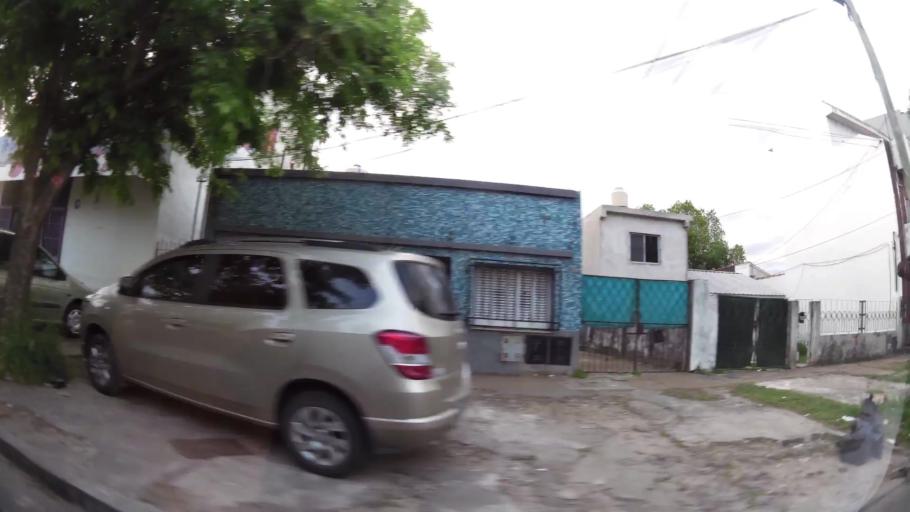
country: AR
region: Buenos Aires
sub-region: Partido de Quilmes
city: Quilmes
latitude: -34.7477
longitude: -58.2362
